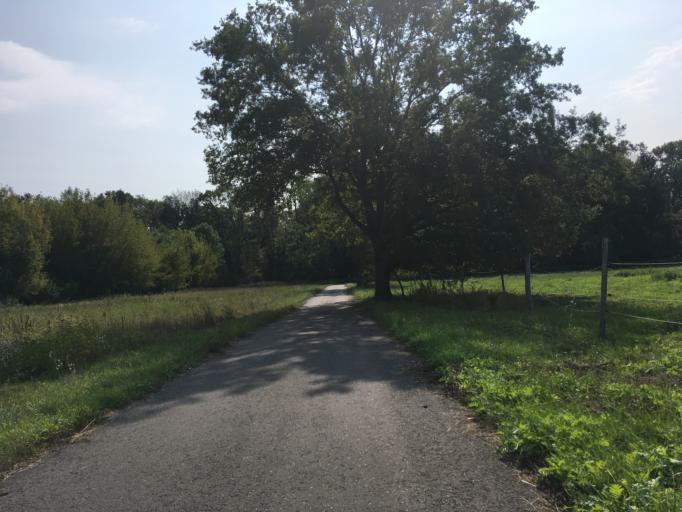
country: DE
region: Berlin
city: Falkenhagener Feld
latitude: 52.5971
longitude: 13.1589
